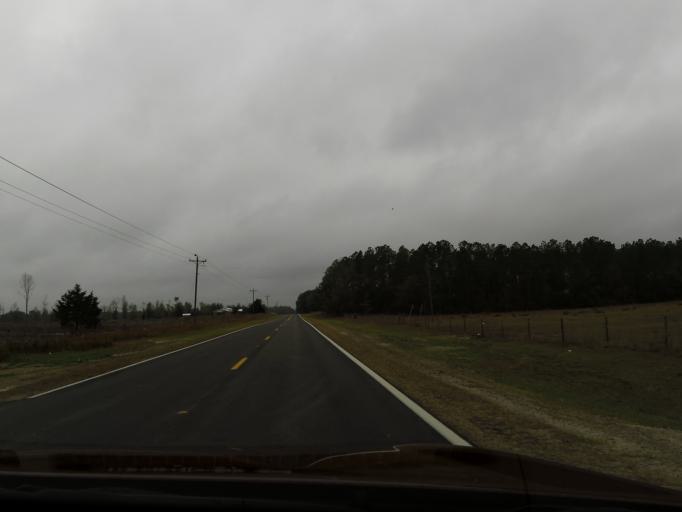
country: US
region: Florida
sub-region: Gilchrist County
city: Trenton
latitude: 29.7958
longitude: -82.8963
